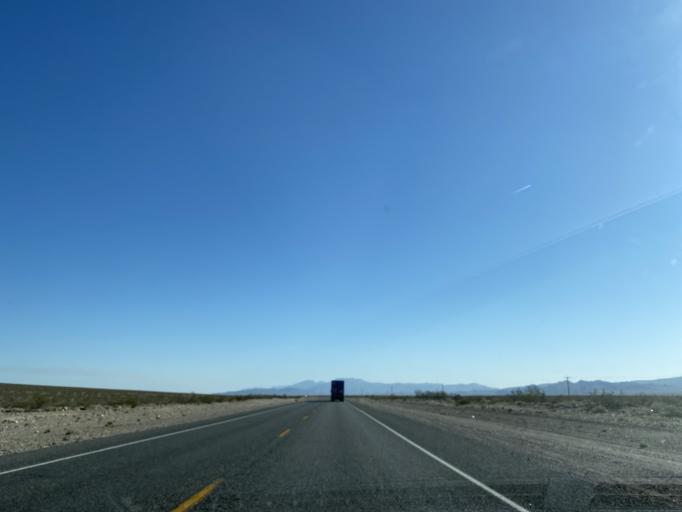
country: US
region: Nevada
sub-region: Nye County
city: Beatty
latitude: 36.8474
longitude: -116.7546
